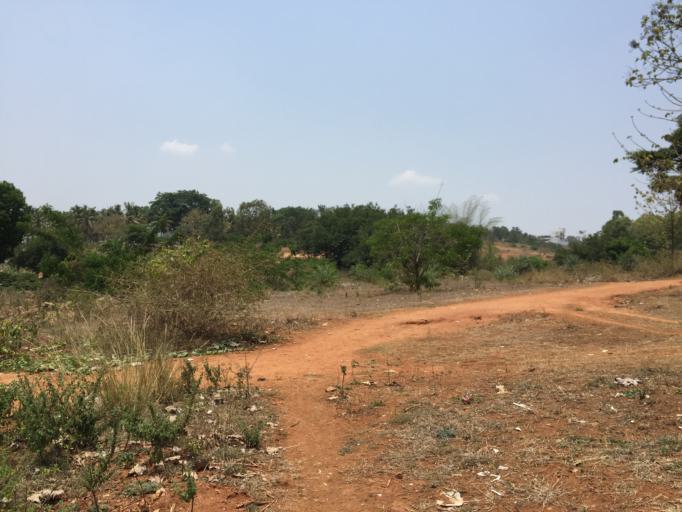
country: IN
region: Karnataka
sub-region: Bangalore Urban
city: Bangalore
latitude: 12.8920
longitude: 77.5305
